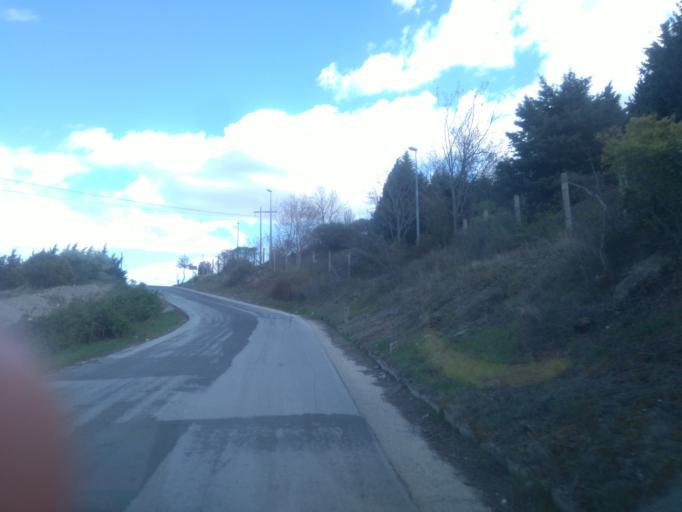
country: GR
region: Central Macedonia
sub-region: Nomos Thessalonikis
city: Asvestochori
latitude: 40.6349
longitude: 23.0213
